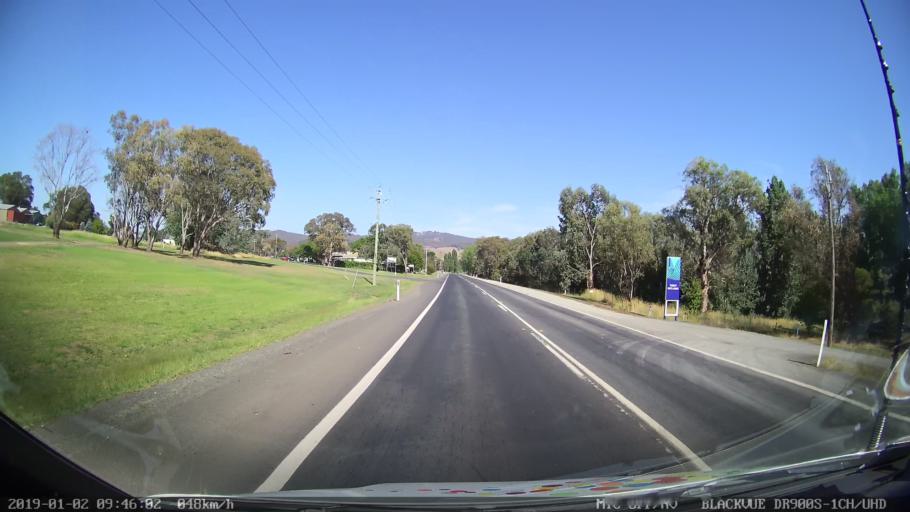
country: AU
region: New South Wales
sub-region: Tumut Shire
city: Tumut
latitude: -35.2942
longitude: 148.2147
